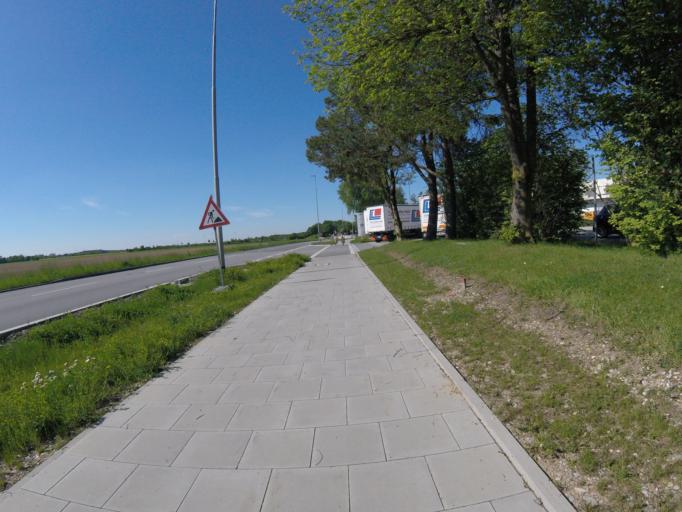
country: DE
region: Bavaria
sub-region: Upper Bavaria
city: Ottobrunn
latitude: 48.0526
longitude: 11.6504
